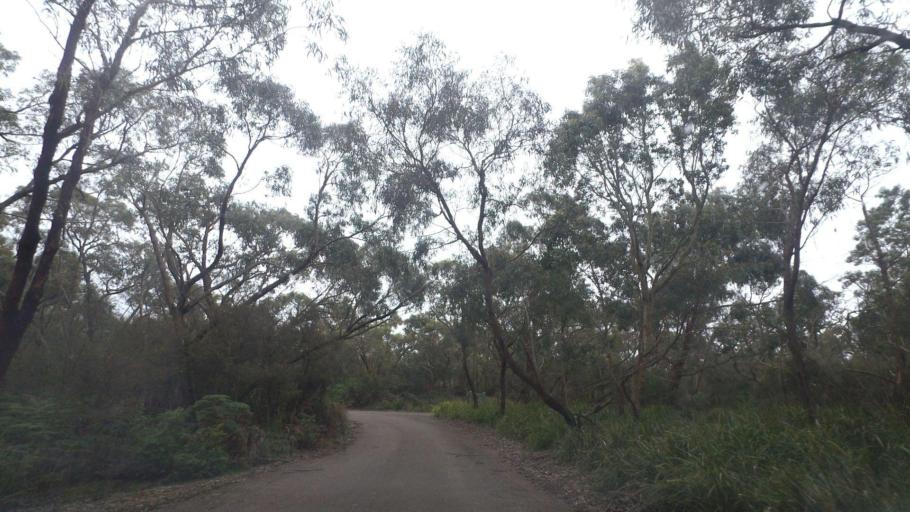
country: AU
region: Victoria
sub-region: Casey
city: Junction Village
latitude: -38.1366
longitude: 145.2831
